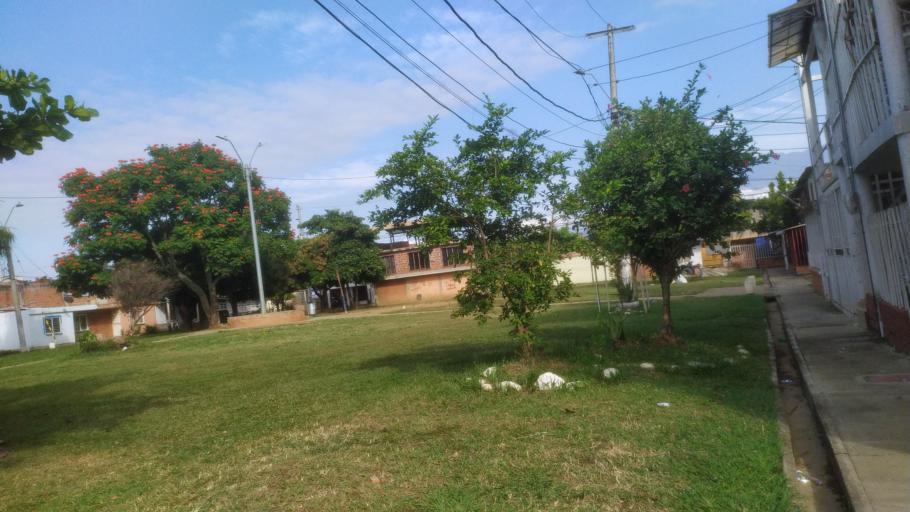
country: CO
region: Valle del Cauca
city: Jamundi
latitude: 3.2399
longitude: -76.5092
